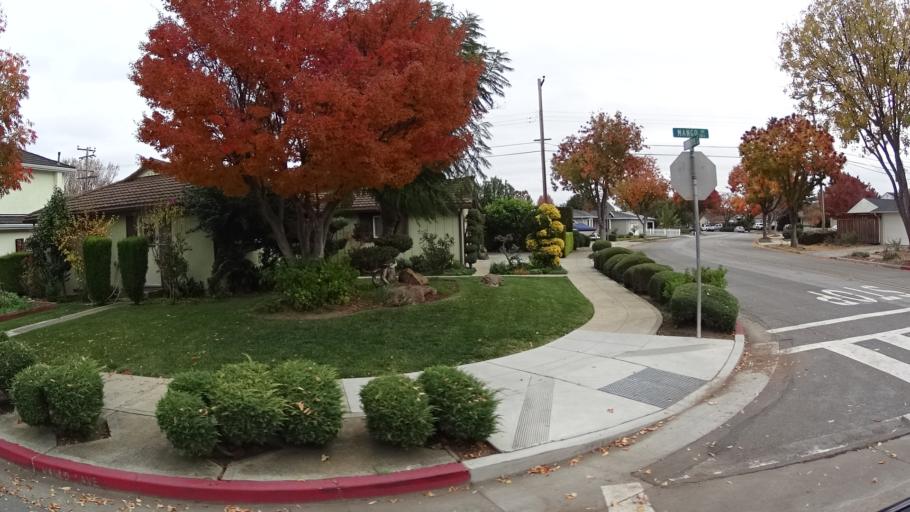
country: US
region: California
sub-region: Santa Clara County
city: Sunnyvale
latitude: 37.3663
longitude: -122.0520
